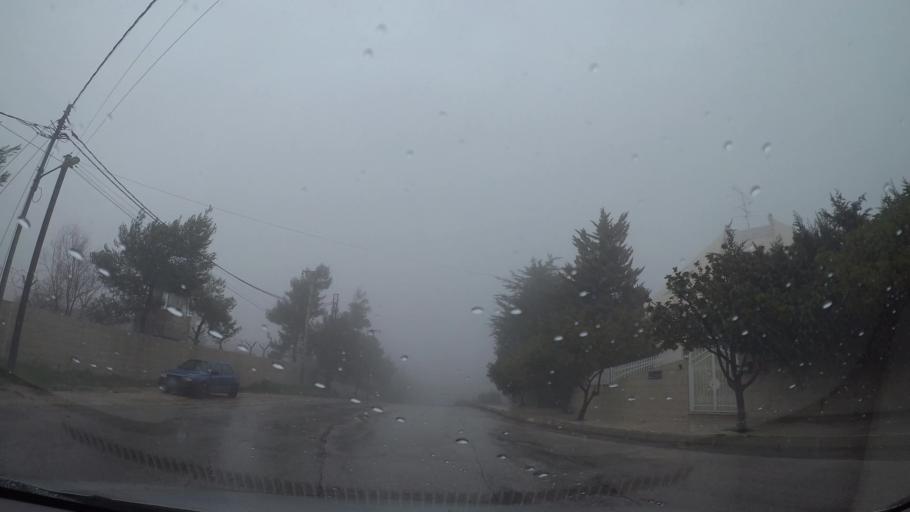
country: JO
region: Amman
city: Wadi as Sir
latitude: 32.0000
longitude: 35.8229
